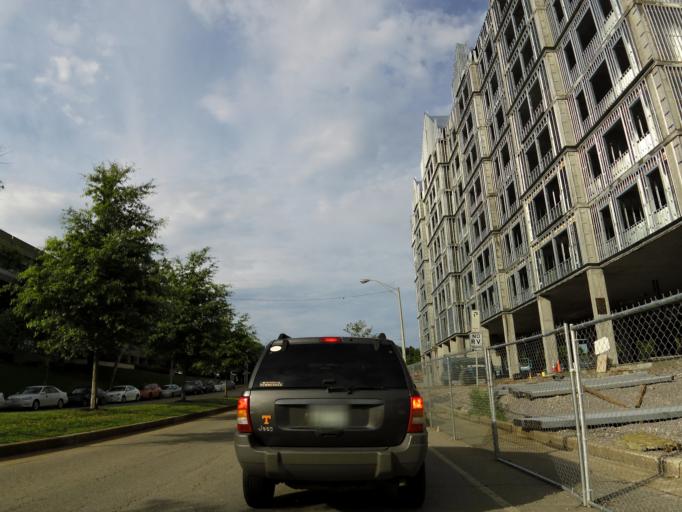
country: US
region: Tennessee
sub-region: Knox County
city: Knoxville
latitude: 35.9517
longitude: -83.9297
